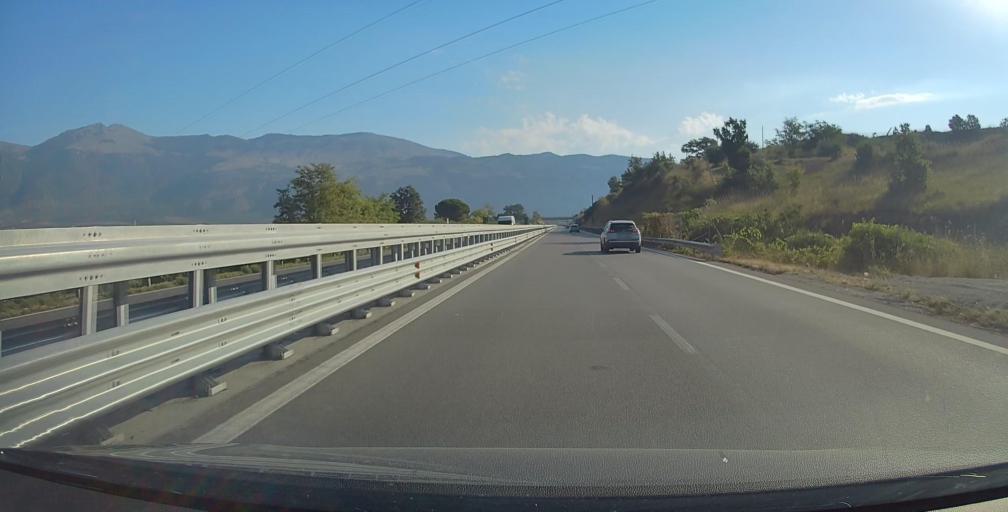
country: IT
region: Calabria
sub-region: Provincia di Cosenza
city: Castrovillari
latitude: 39.8041
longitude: 16.2446
